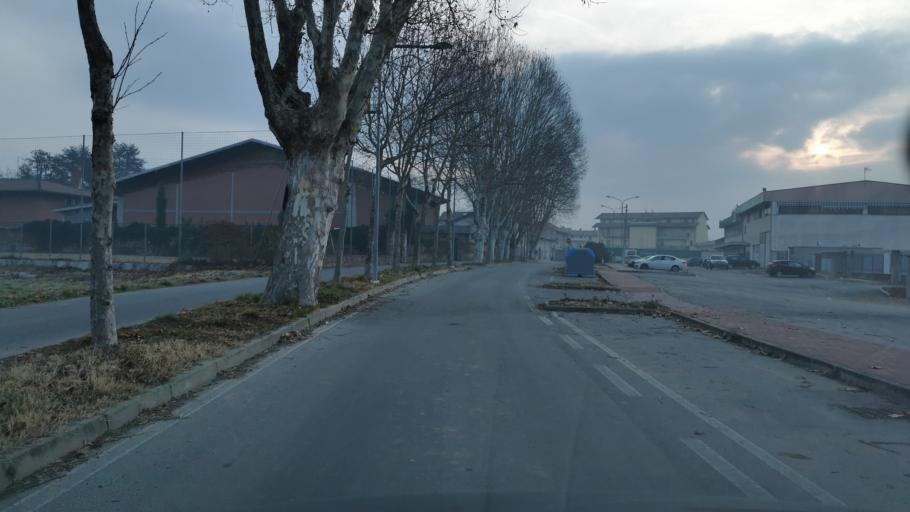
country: IT
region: Piedmont
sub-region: Provincia di Torino
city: San Giorgio Canavese
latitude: 45.3333
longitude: 7.7920
